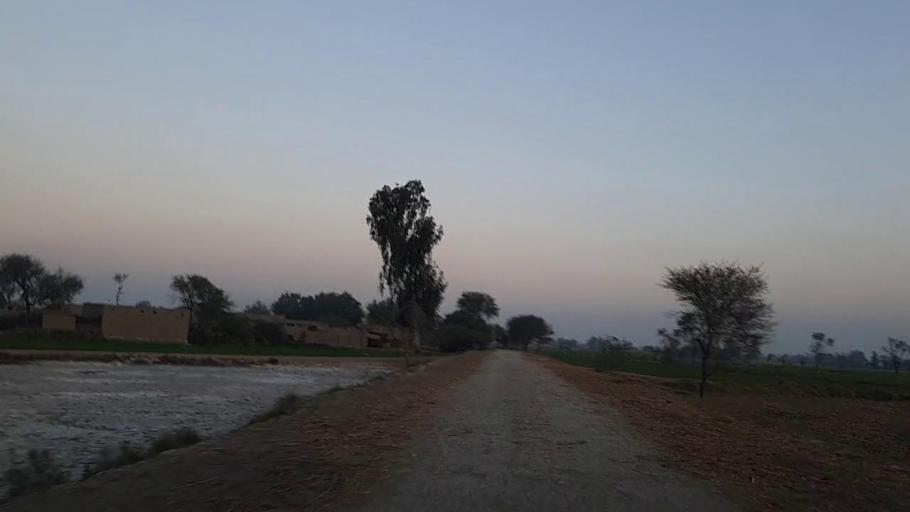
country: PK
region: Sindh
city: Naushahro Firoz
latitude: 26.7912
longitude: 68.0424
